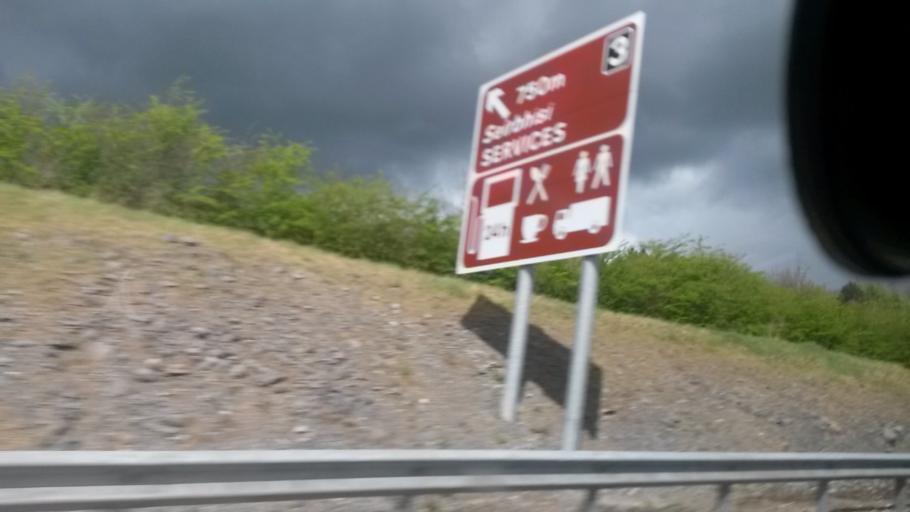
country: IE
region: Leinster
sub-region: Laois
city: Rathdowney
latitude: 52.8537
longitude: -7.4895
